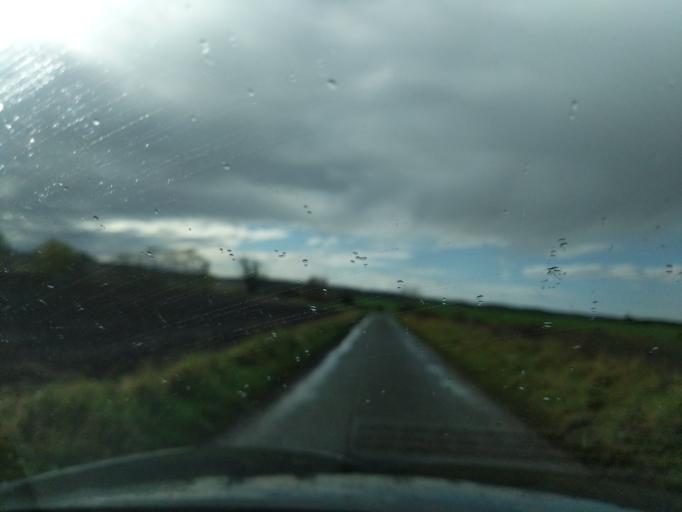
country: GB
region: Scotland
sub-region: Fife
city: Saint Andrews
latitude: 56.3017
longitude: -2.7394
